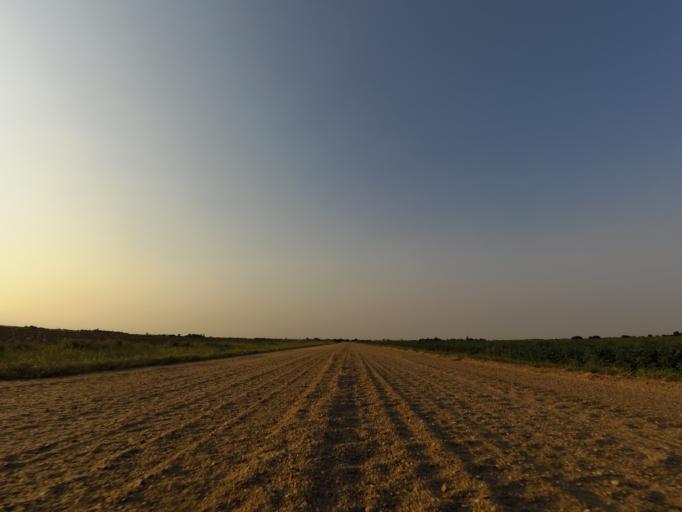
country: US
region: Kansas
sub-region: Reno County
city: South Hutchinson
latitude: 37.9717
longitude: -97.9957
